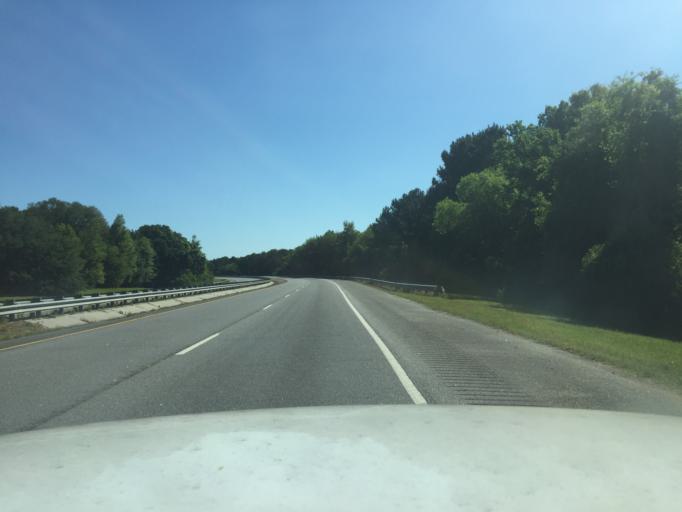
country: US
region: Georgia
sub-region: Chatham County
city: Georgetown
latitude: 32.0139
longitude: -81.1786
